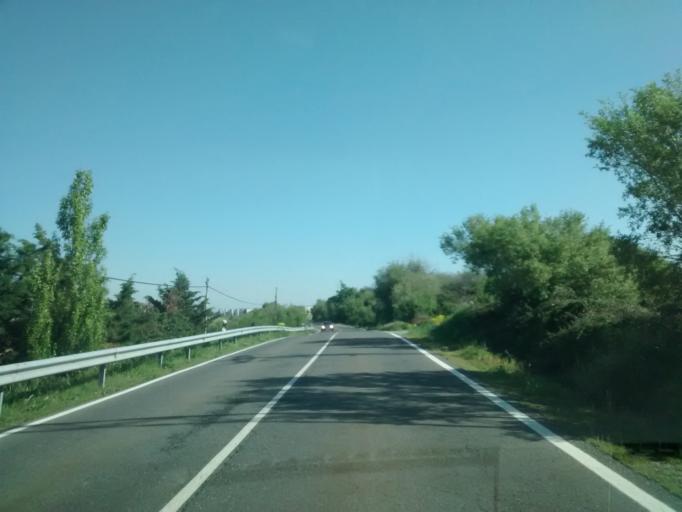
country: ES
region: Castille and Leon
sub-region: Provincia de Segovia
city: Trescasas
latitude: 40.9414
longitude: -4.0335
